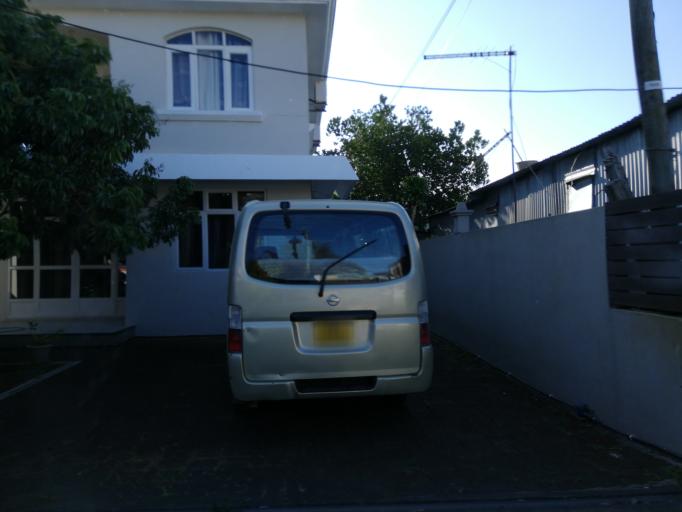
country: MU
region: Moka
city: Saint Pierre
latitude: -20.2158
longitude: 57.5239
